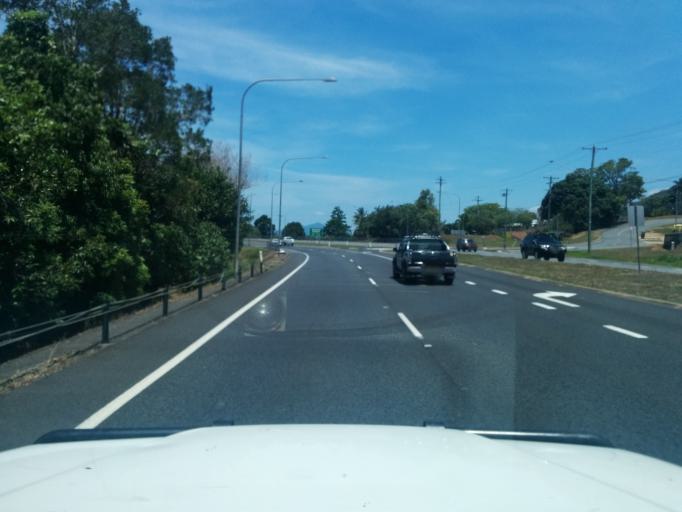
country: AU
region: Queensland
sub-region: Cairns
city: Redlynch
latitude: -16.9120
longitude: 145.7168
